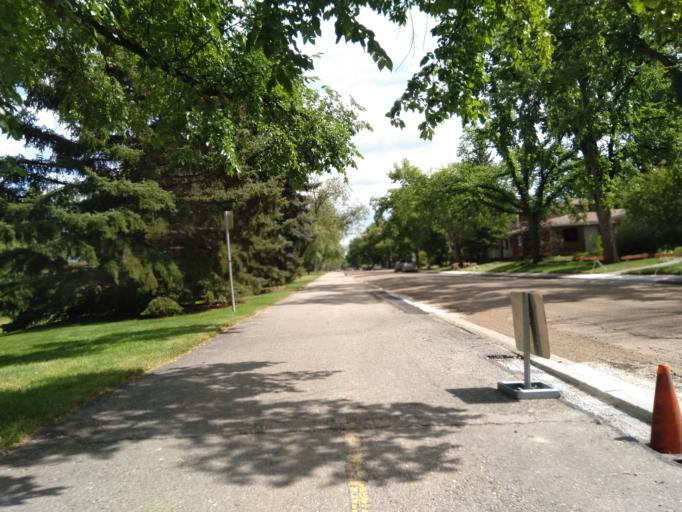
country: CA
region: Alberta
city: Calgary
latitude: 51.0808
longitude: -114.1139
